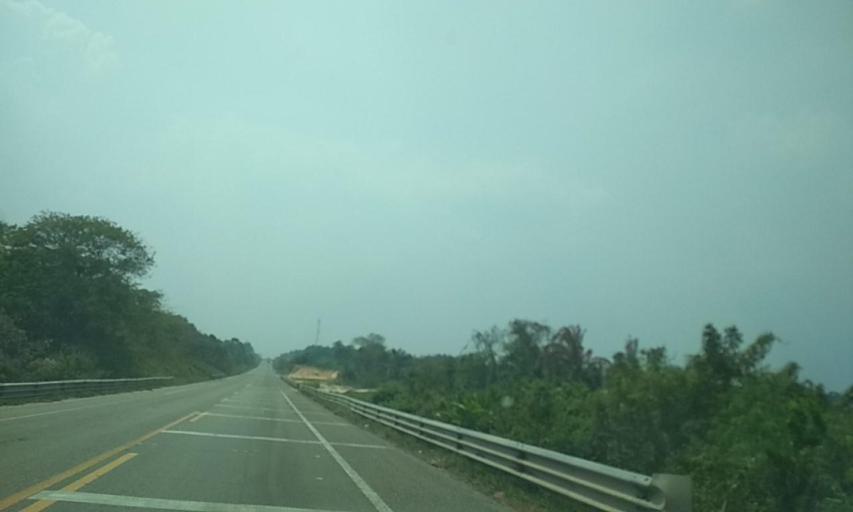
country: MX
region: Tabasco
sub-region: Huimanguillo
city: Francisco Rueda
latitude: 17.7431
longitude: -93.9849
